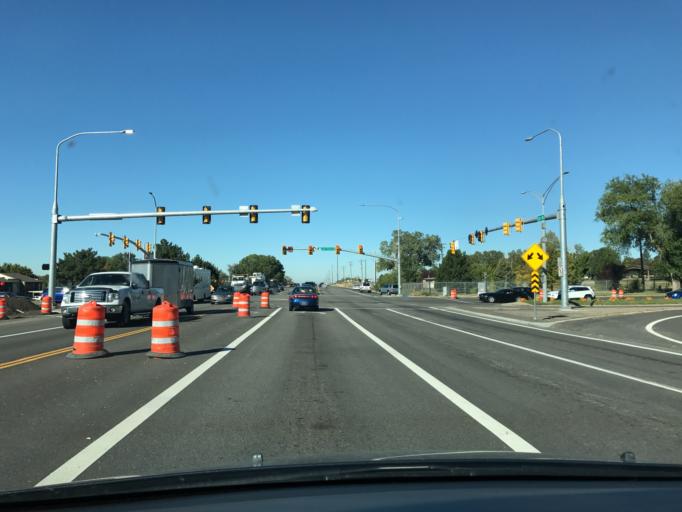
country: US
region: Utah
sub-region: Davis County
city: Hill Air Force Bace
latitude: 41.1035
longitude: -111.9727
